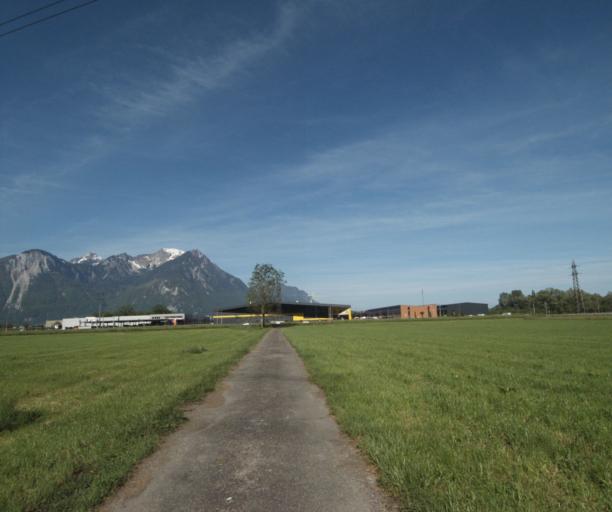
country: CH
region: Vaud
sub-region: Aigle District
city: Villeneuve
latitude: 46.3831
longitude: 6.9313
